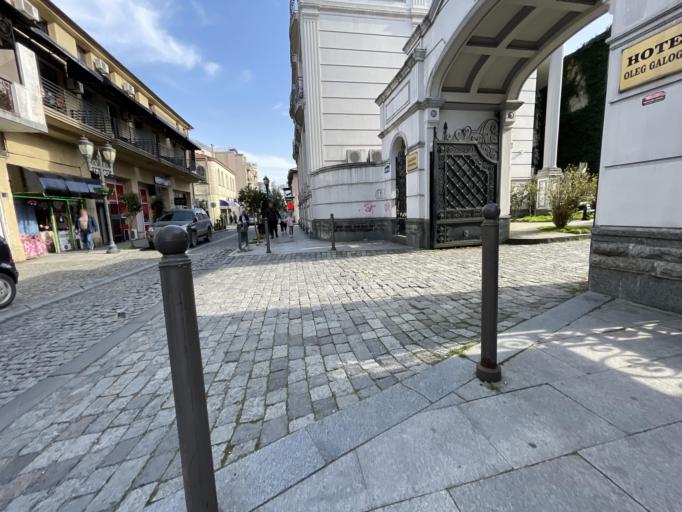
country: GE
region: Ajaria
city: Batumi
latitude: 41.6499
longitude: 41.6419
